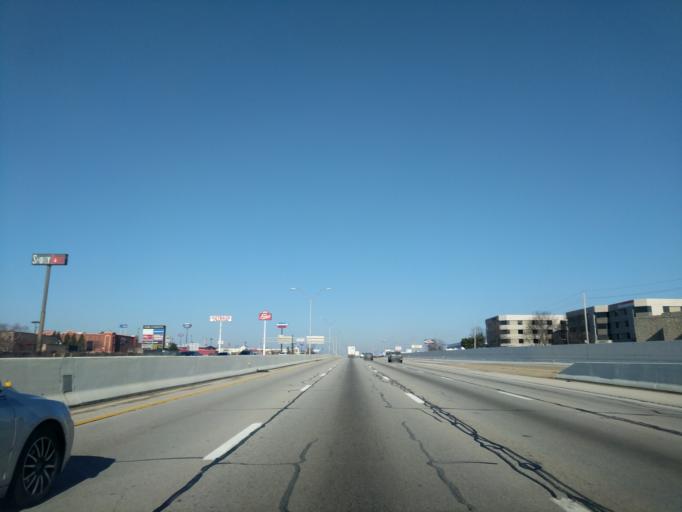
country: US
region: Ohio
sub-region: Montgomery County
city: Northridge
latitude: 39.8440
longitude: -84.1897
